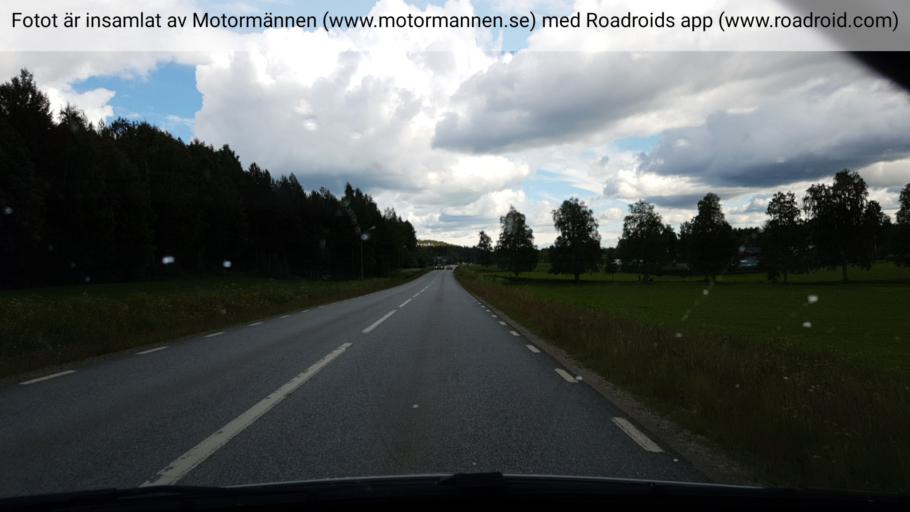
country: SE
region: Vaesterbotten
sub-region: Bjurholms Kommun
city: Bjurholm
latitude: 64.2380
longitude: 19.3400
